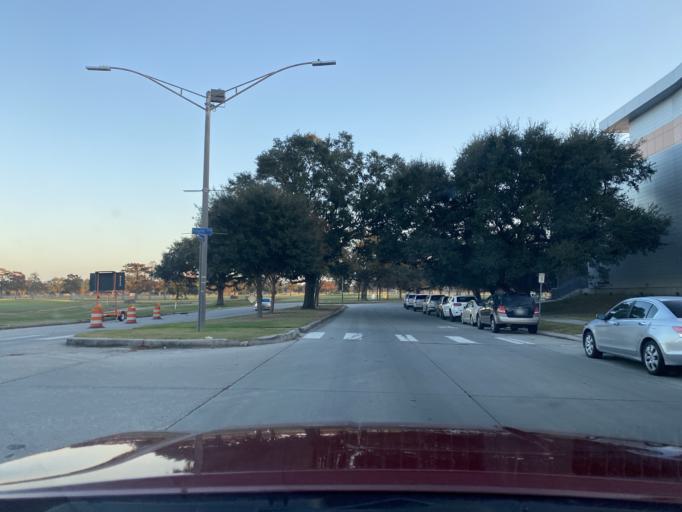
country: US
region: Louisiana
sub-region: Orleans Parish
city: New Orleans
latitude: 30.0272
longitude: -90.0441
